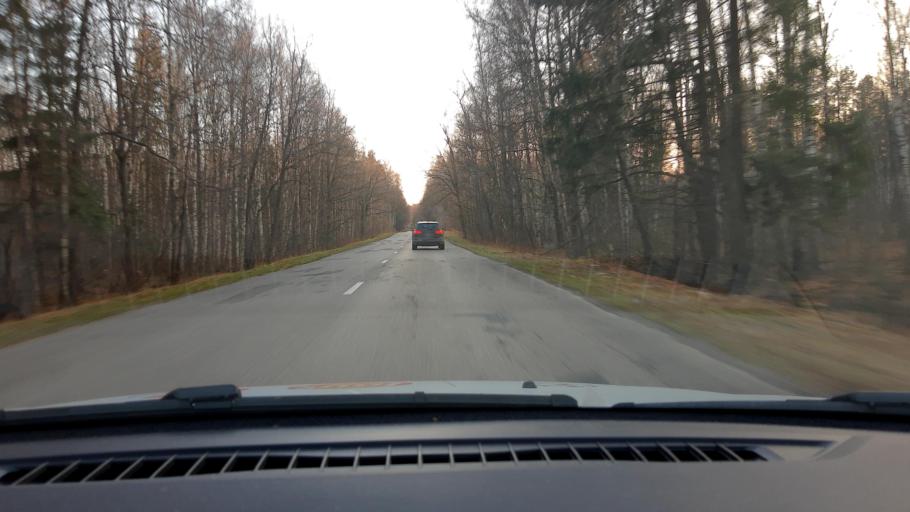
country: RU
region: Nizjnij Novgorod
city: Volodarsk
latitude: 56.2643
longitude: 43.1682
